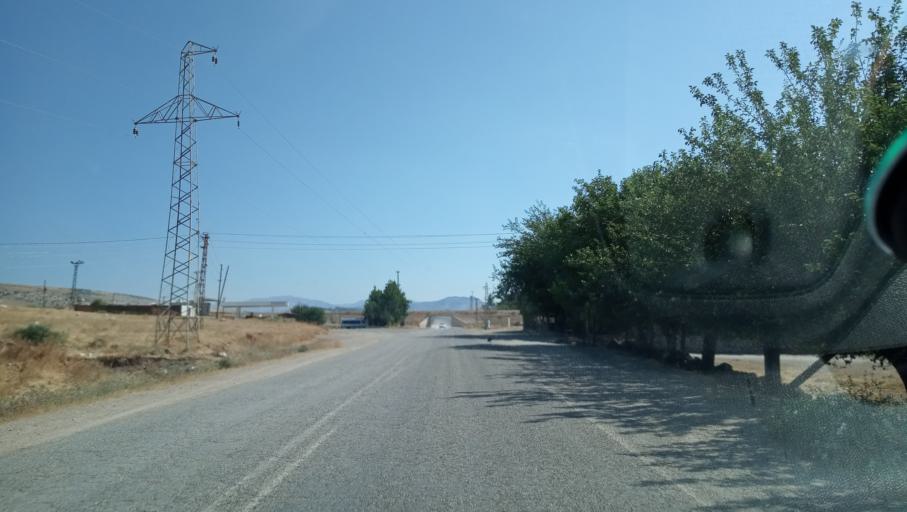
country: TR
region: Diyarbakir
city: Malabadi
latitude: 38.1359
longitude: 41.1902
